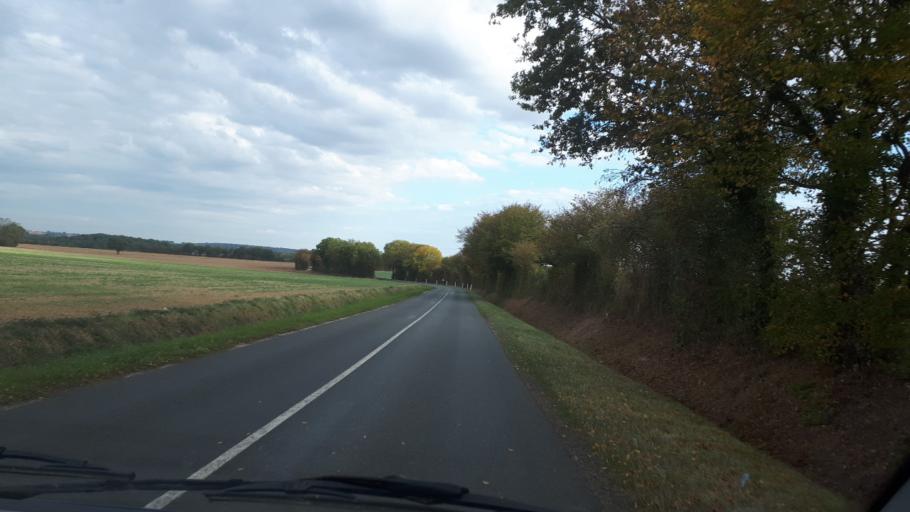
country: FR
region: Centre
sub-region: Departement du Loir-et-Cher
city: Mondoubleau
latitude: 48.0509
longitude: 0.9440
